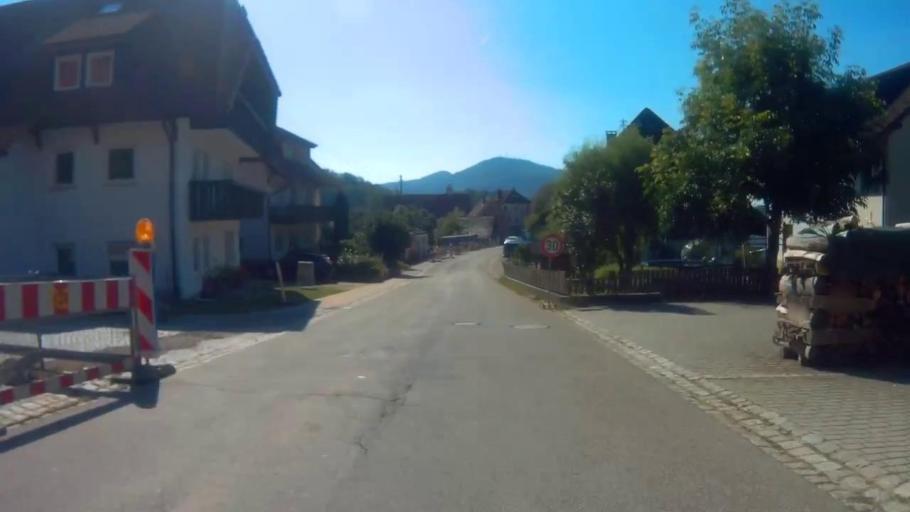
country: DE
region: Baden-Wuerttemberg
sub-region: Freiburg Region
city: Zell im Wiesental
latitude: 47.7171
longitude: 7.8369
